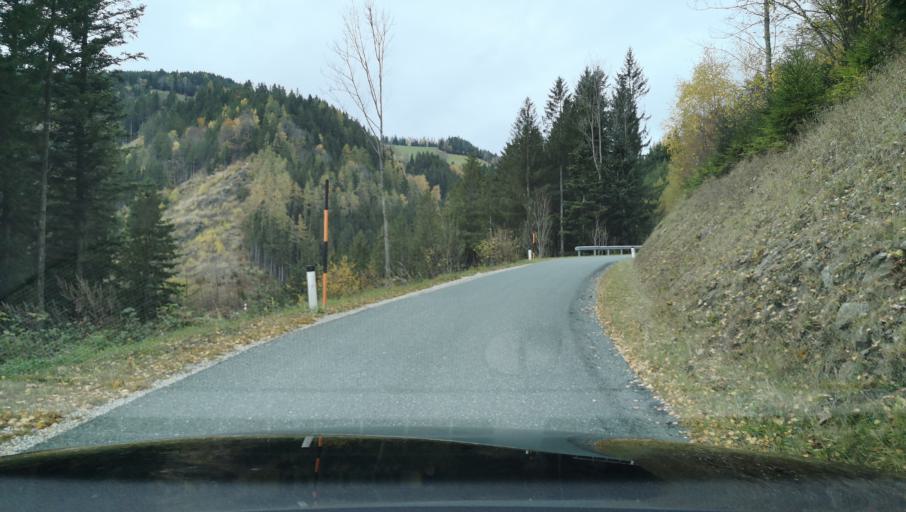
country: AT
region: Styria
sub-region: Politischer Bezirk Weiz
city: Birkfeld
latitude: 47.3664
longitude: 15.6320
